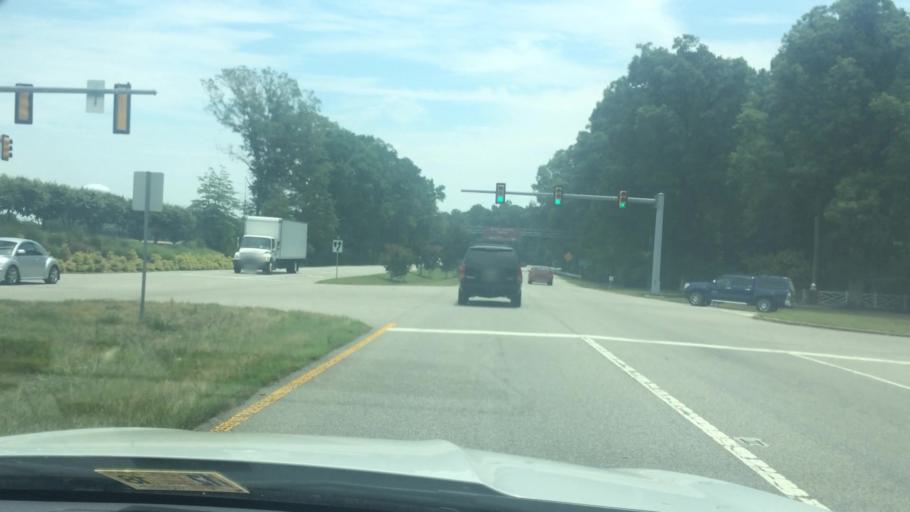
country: US
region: Virginia
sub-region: City of Williamsburg
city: Williamsburg
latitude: 37.2437
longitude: -76.6559
